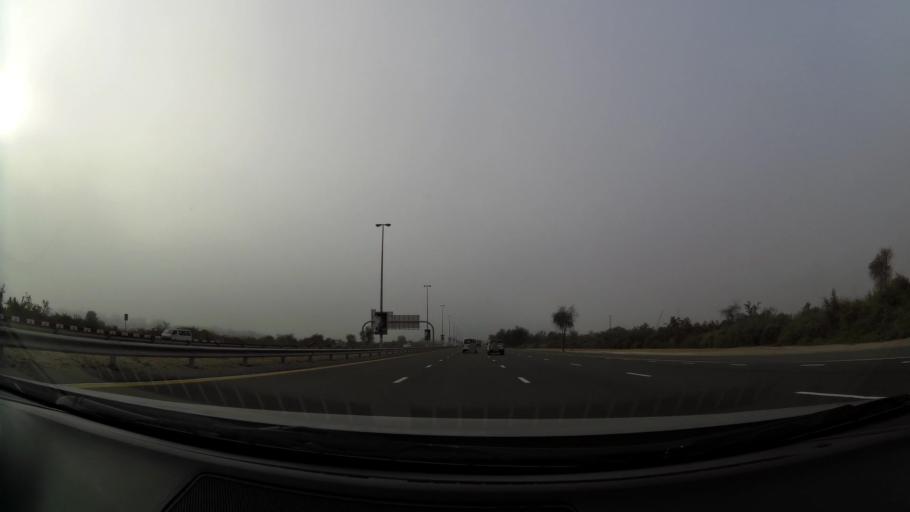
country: AE
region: Dubai
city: Dubai
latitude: 25.1664
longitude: 55.3271
